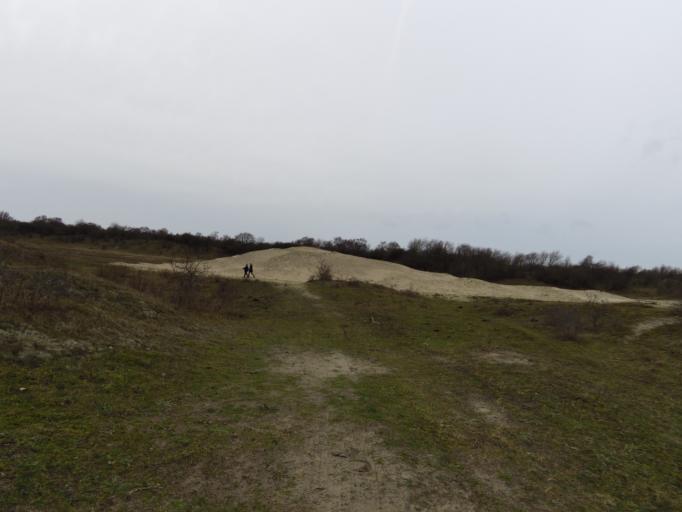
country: NL
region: South Holland
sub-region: Gemeente Rotterdam
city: Hoek van Holland
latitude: 51.9120
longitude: 4.0706
